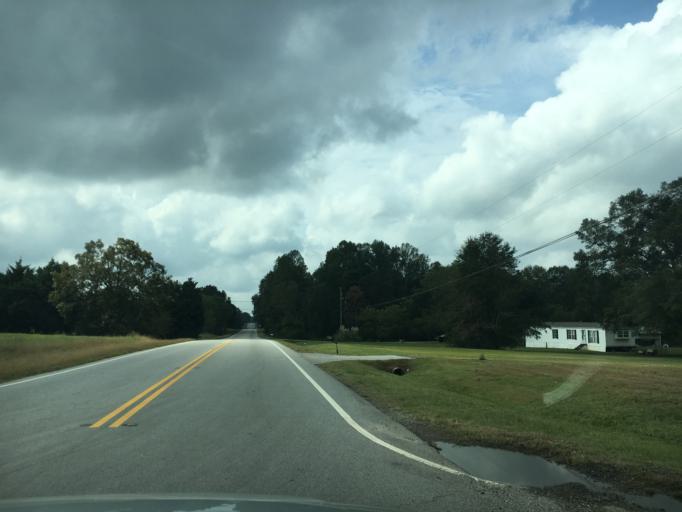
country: US
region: Georgia
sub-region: Hart County
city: Royston
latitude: 34.3608
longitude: -83.0973
